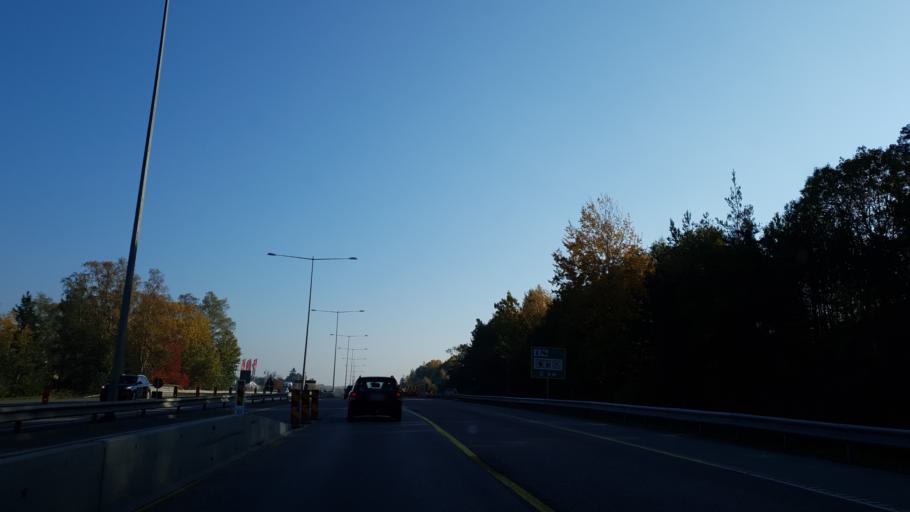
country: SE
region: Stockholm
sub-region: Haninge Kommun
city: Handen
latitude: 59.1948
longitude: 18.1373
